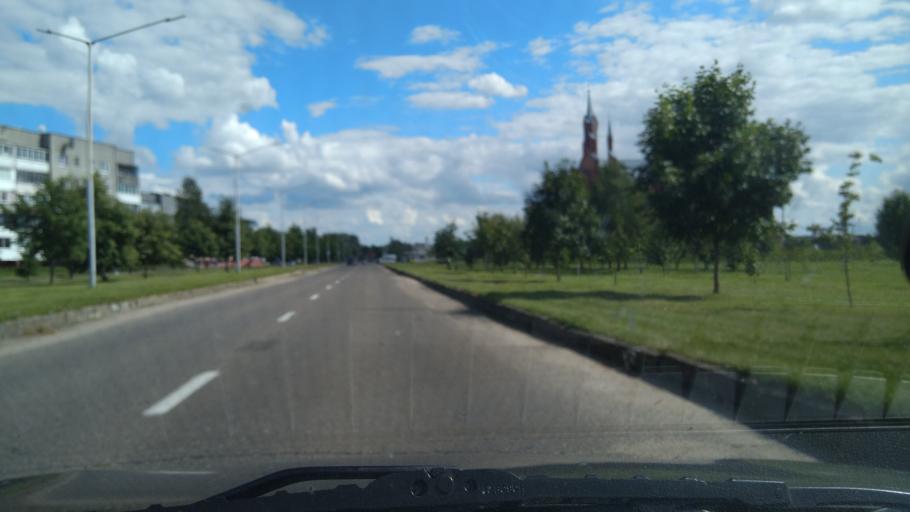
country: BY
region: Grodnenskaya
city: Masty
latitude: 53.4202
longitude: 24.5403
